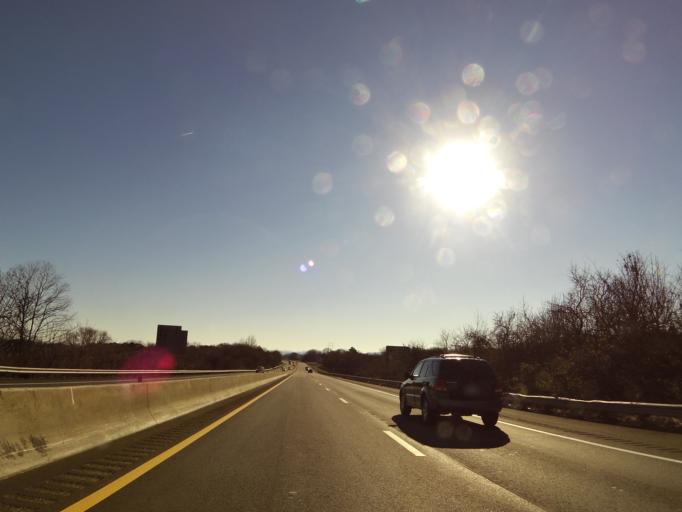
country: US
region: Tennessee
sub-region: Jefferson County
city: White Pine
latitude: 36.0394
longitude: -83.3329
